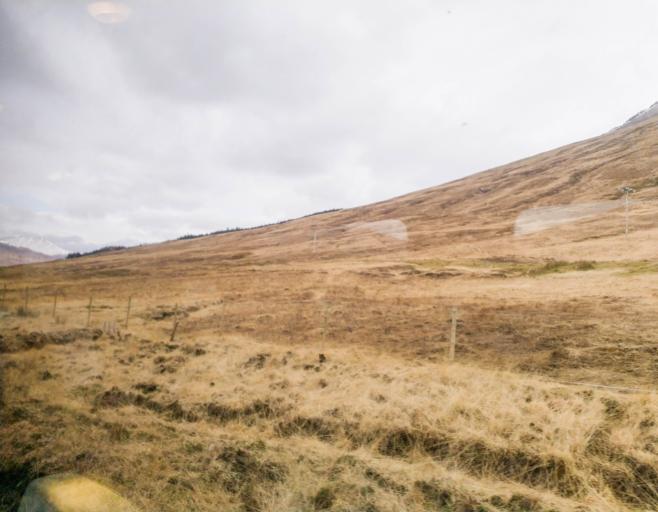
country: GB
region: Scotland
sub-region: Argyll and Bute
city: Garelochhead
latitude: 56.4985
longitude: -4.7480
